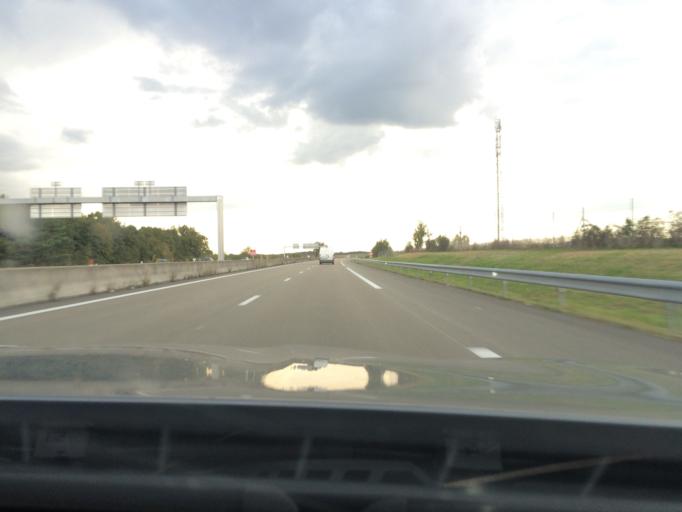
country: FR
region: Ile-de-France
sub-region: Departement de Seine-et-Marne
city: Souppes-sur-Loing
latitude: 48.2195
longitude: 2.7704
